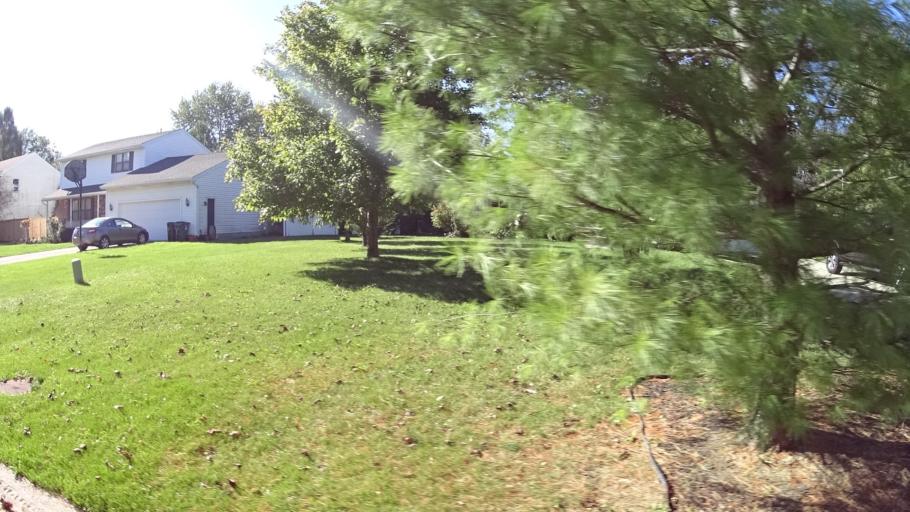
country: US
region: Ohio
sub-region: Lorain County
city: Amherst
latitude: 41.3993
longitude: -82.1922
